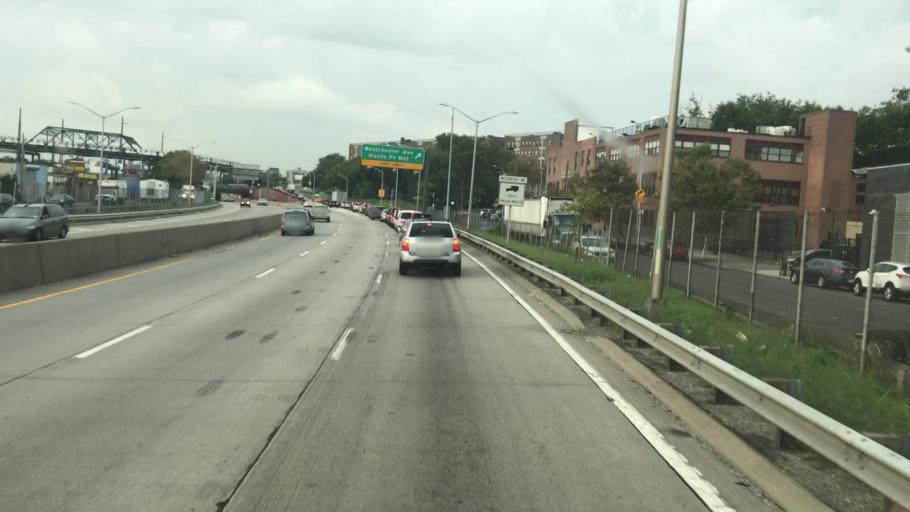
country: US
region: New York
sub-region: Bronx
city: The Bronx
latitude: 40.8318
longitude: -73.8849
